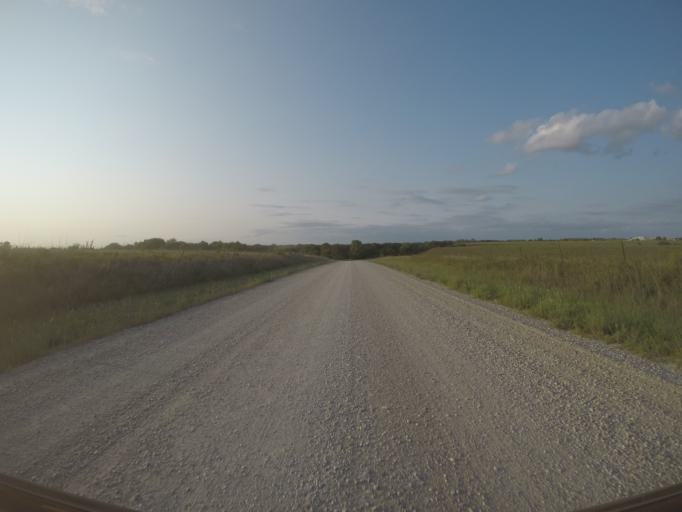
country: US
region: Kansas
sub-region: Pottawatomie County
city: Wamego
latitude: 39.1289
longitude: -96.4280
